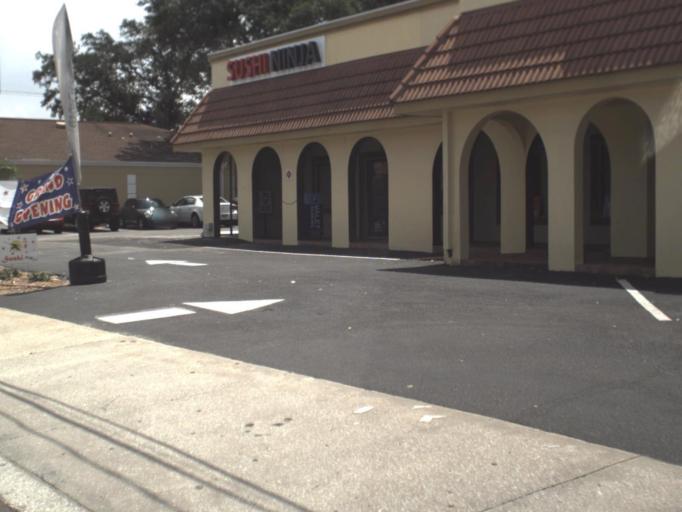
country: US
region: Florida
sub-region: Hillsborough County
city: Tampa
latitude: 27.9447
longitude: -82.4919
